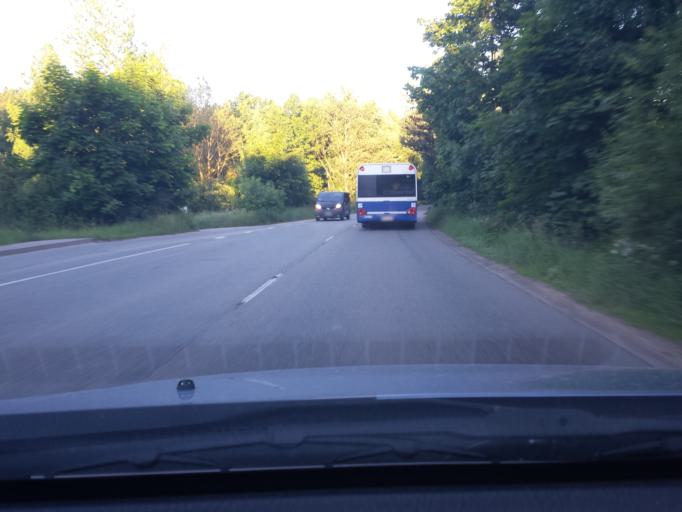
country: LV
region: Riga
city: Jaunciems
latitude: 57.0523
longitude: 24.1693
